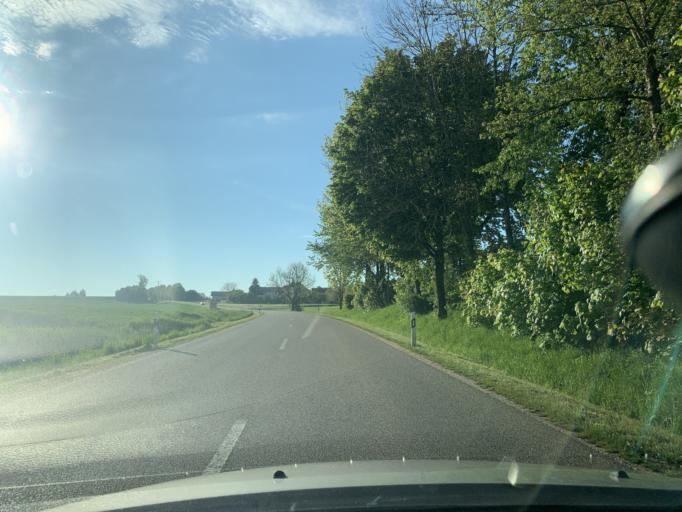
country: DE
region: Bavaria
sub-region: Lower Bavaria
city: Adlkofen
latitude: 48.5279
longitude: 12.2635
